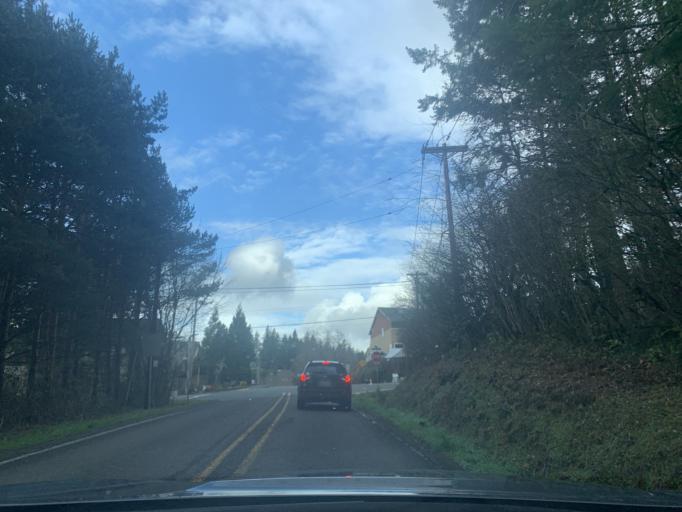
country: US
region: Oregon
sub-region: Washington County
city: Cedar Mill
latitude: 45.5552
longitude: -122.8081
